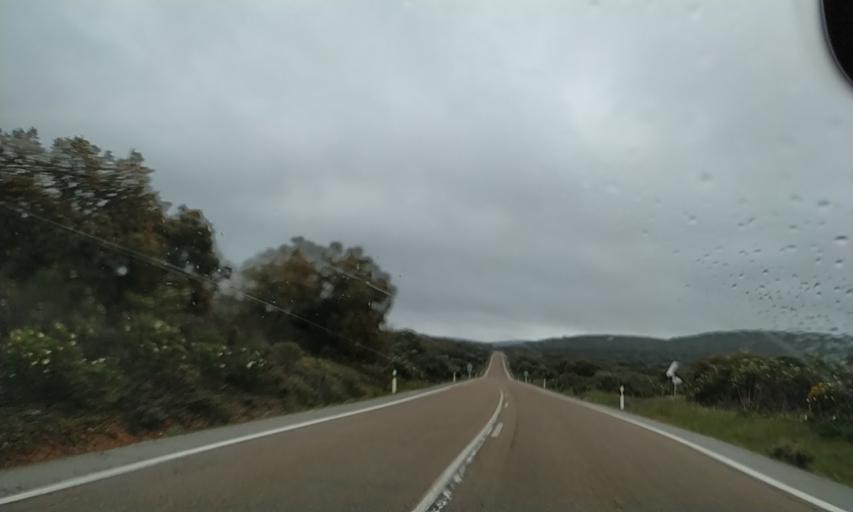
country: ES
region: Extremadura
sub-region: Provincia de Badajoz
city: Puebla de Obando
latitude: 39.2904
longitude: -6.5223
